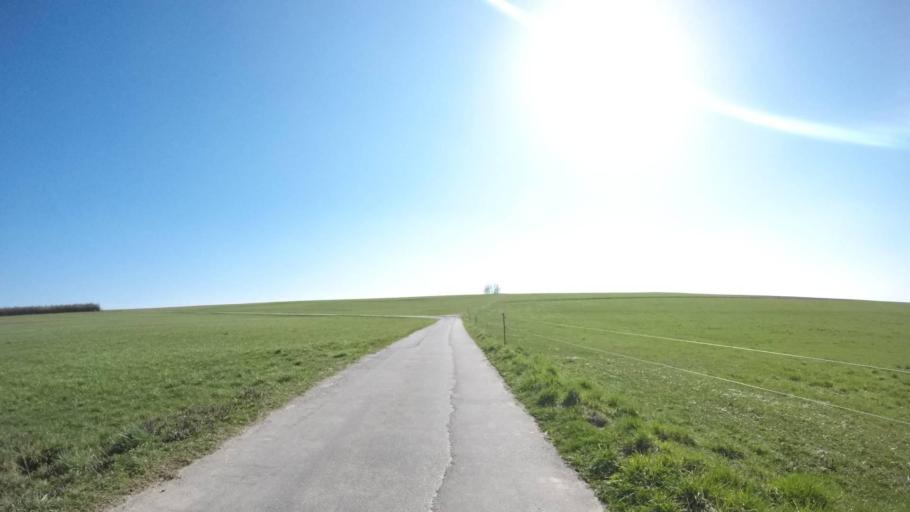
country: DE
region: Saxony
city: Niederfrohna
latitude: 50.8857
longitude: 12.6929
